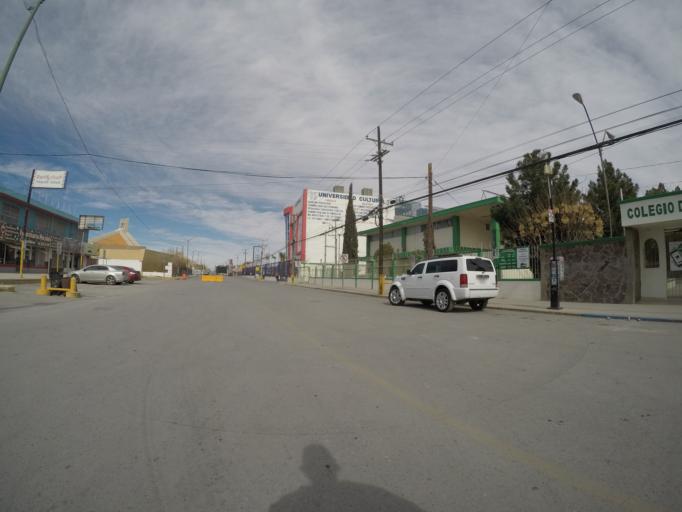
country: MX
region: Chihuahua
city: Ciudad Juarez
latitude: 31.7190
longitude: -106.4318
